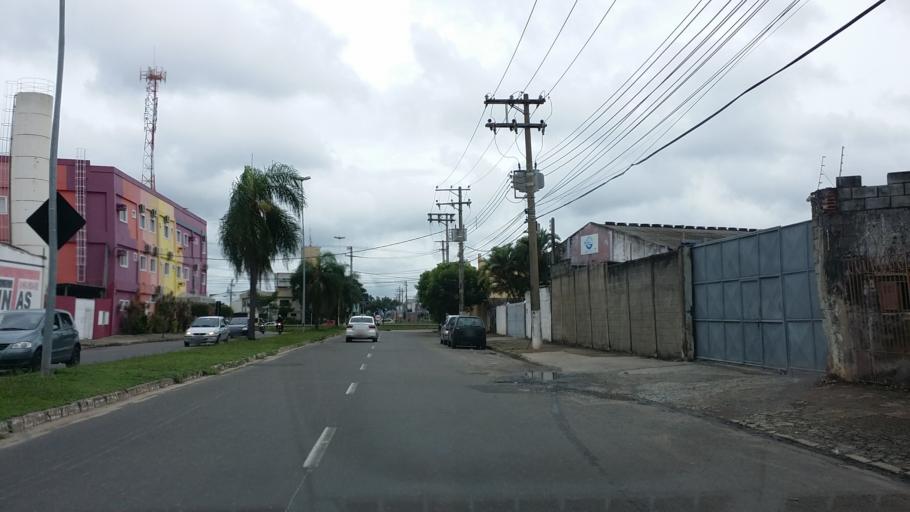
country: BR
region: Sao Paulo
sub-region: Indaiatuba
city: Indaiatuba
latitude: -23.1210
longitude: -47.2240
